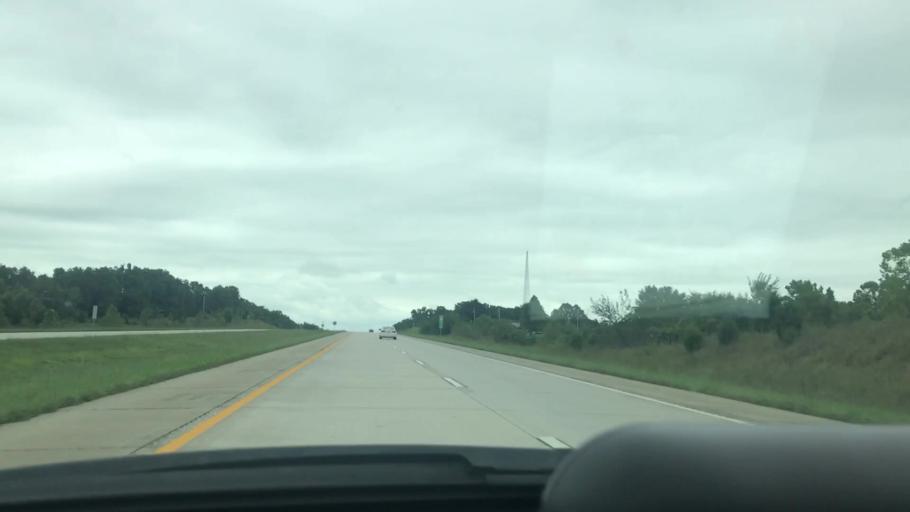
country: US
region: Missouri
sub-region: Dallas County
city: Buffalo
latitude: 37.5372
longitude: -93.1373
